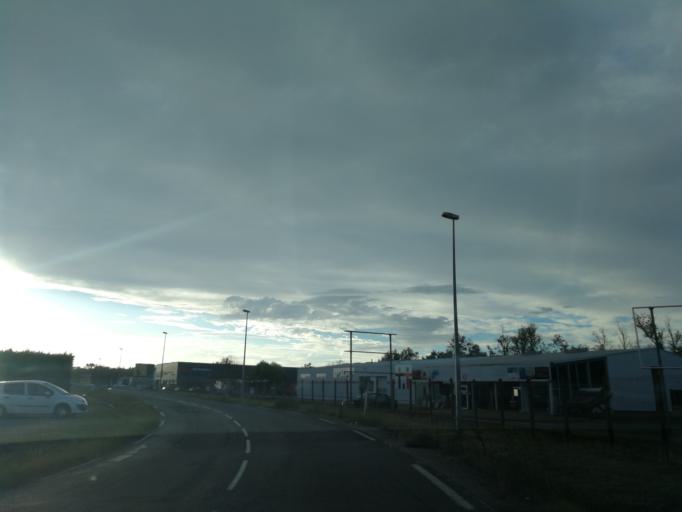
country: FR
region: Midi-Pyrenees
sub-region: Departement de la Haute-Garonne
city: Launaguet
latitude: 43.6639
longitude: 1.4628
